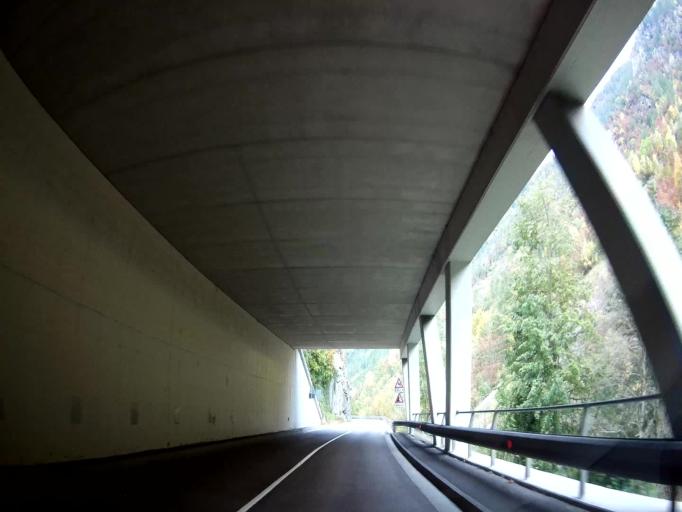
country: IT
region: Trentino-Alto Adige
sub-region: Bolzano
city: Naturno
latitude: 46.6649
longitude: 10.9519
